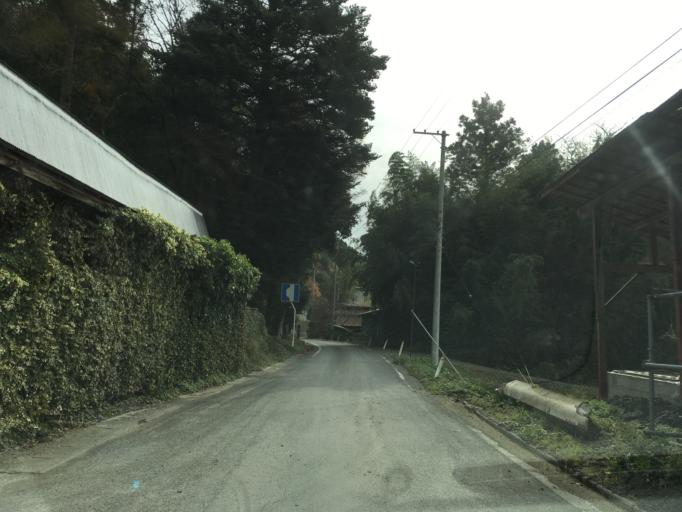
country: JP
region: Iwate
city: Ichinoseki
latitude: 38.7809
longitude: 141.2677
